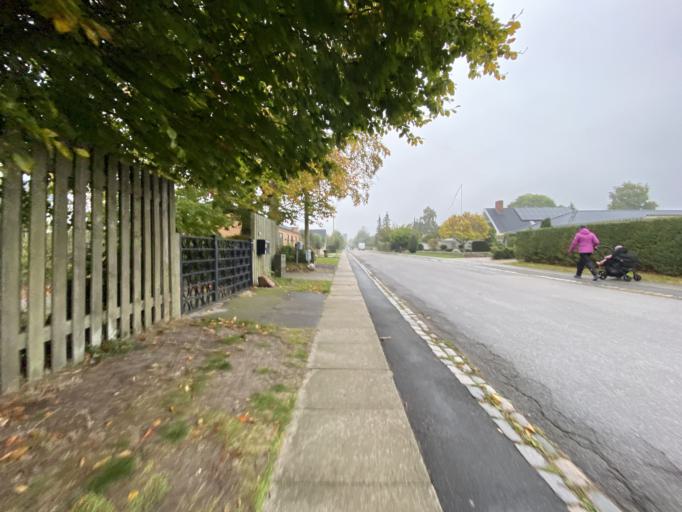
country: DK
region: Capital Region
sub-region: Dragor Kommune
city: Dragor
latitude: 55.5860
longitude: 12.6506
